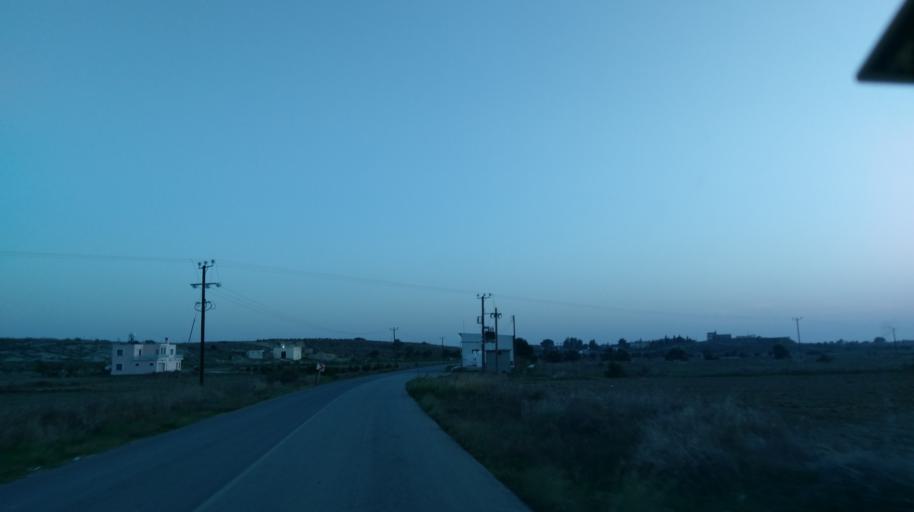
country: CY
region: Ammochostos
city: Trikomo
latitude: 35.2967
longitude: 33.8914
